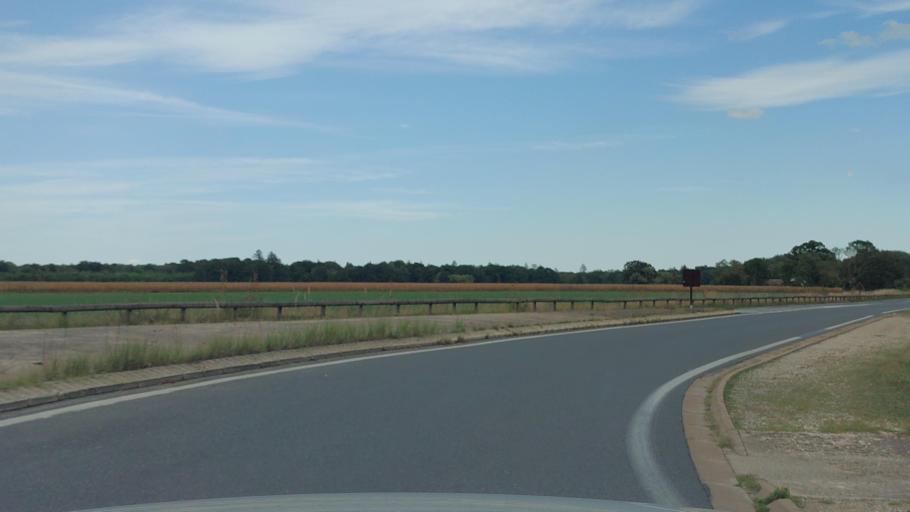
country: FR
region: Ile-de-France
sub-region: Departement de Seine-et-Marne
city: Le Chatelet-en-Brie
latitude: 48.5436
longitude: 2.7987
